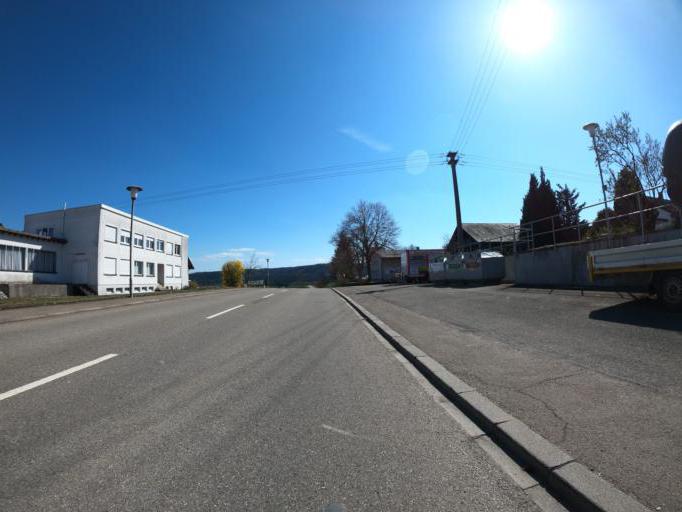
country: DE
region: Baden-Wuerttemberg
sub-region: Tuebingen Region
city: Rangendingen
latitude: 48.3868
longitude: 8.8474
